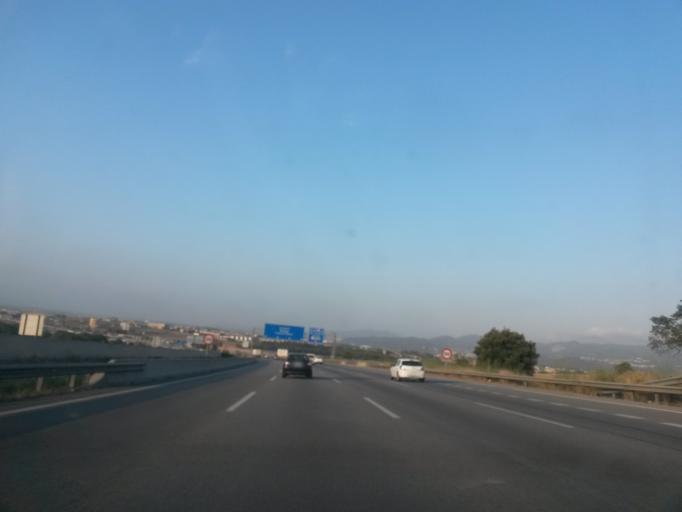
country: ES
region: Catalonia
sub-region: Provincia de Barcelona
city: Ripollet
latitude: 41.5212
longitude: 2.1590
